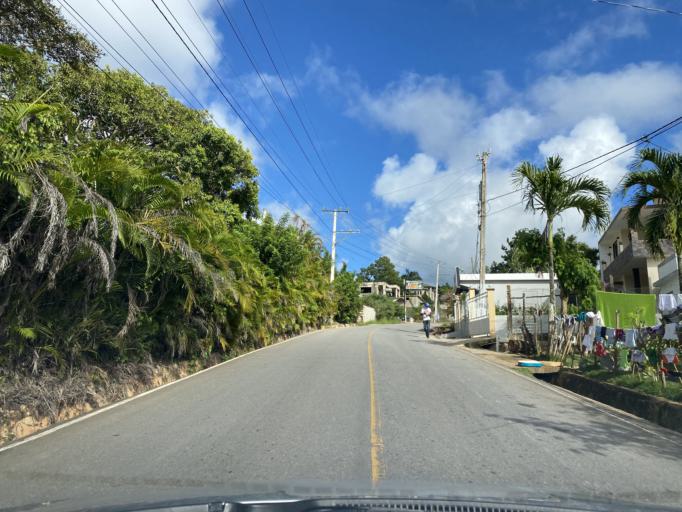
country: DO
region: Samana
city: Las Terrenas
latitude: 19.2706
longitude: -69.5576
